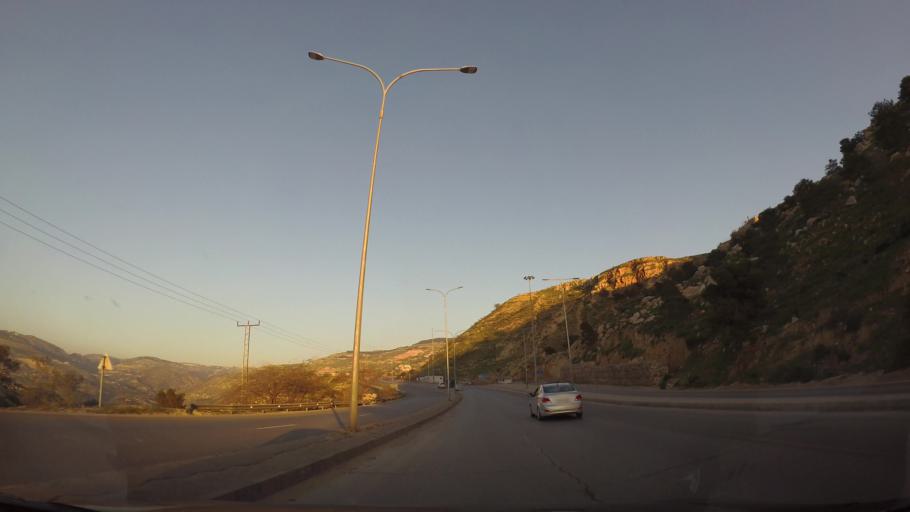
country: JO
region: Amman
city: Umm as Summaq
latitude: 31.8687
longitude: 35.7427
